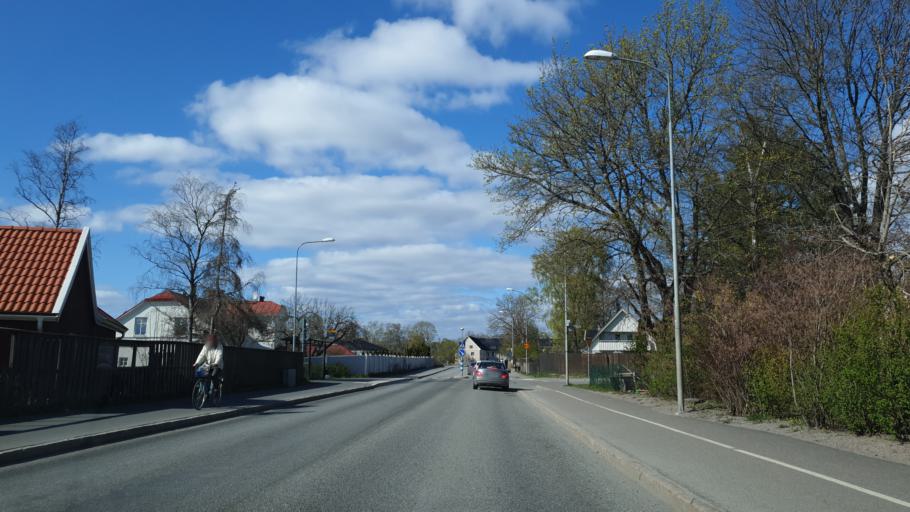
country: SE
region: Uppsala
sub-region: Uppsala Kommun
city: Gamla Uppsala
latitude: 59.8943
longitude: 17.6373
